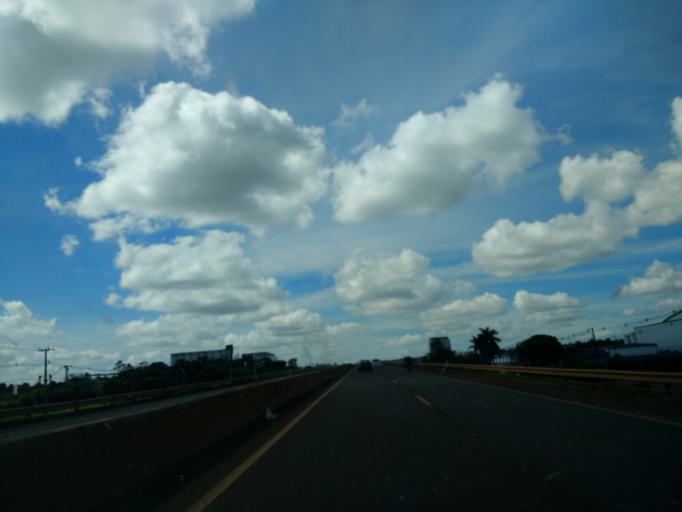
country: BR
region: Parana
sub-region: Paicandu
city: Paicandu
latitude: -23.4516
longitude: -52.0078
